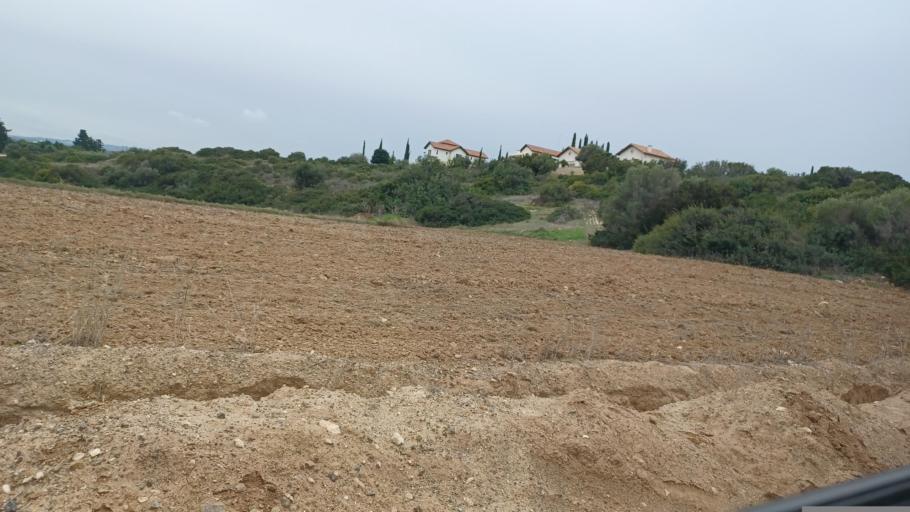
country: CY
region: Pafos
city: Polis
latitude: 35.0422
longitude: 32.3769
